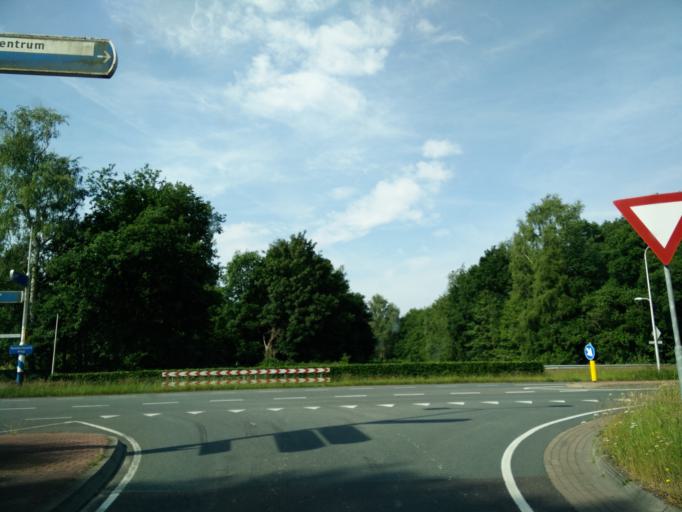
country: NL
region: Drenthe
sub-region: Gemeente Assen
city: Assen
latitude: 52.9918
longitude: 6.5926
